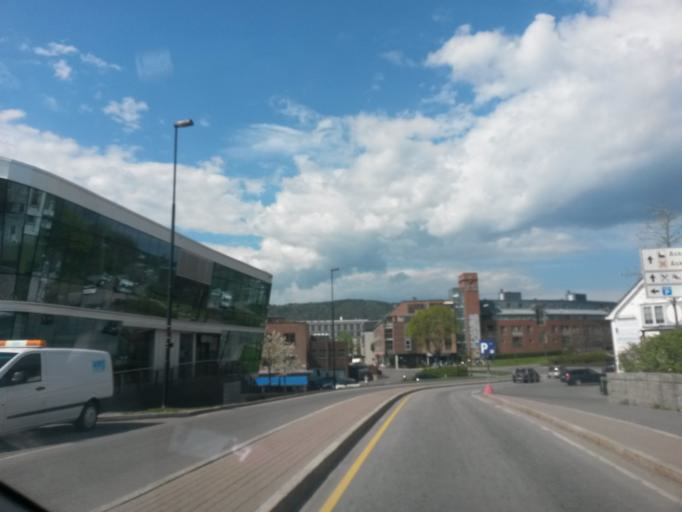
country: NO
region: Akershus
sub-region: Asker
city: Asker
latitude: 59.8348
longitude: 10.4366
